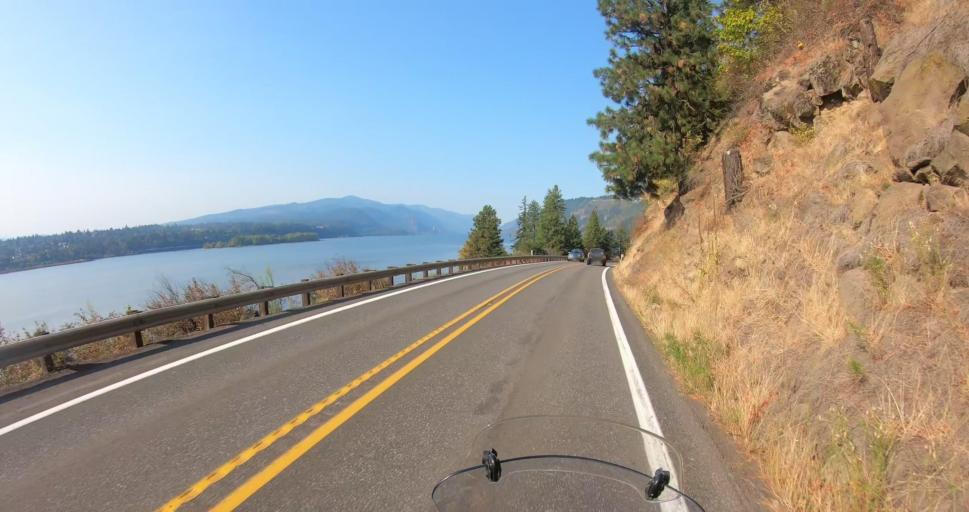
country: US
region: Oregon
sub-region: Hood River County
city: Hood River
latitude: 45.7277
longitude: -121.5170
